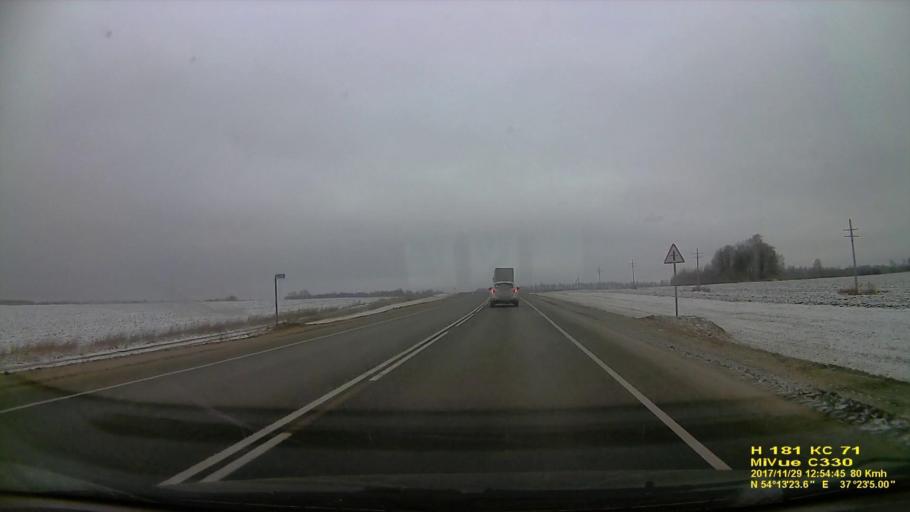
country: RU
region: Tula
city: Leninskiy
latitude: 54.2233
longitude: 37.3846
